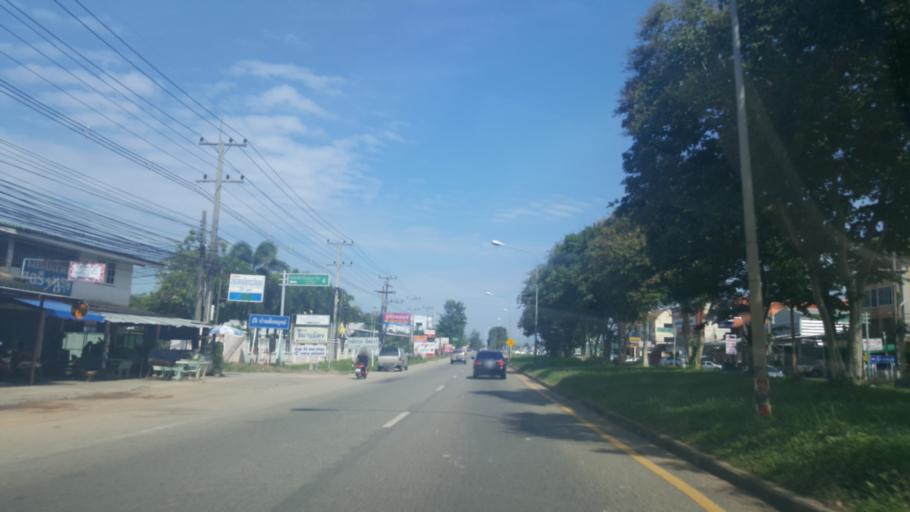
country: TH
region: Chon Buri
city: Sattahip
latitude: 12.7072
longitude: 100.8893
